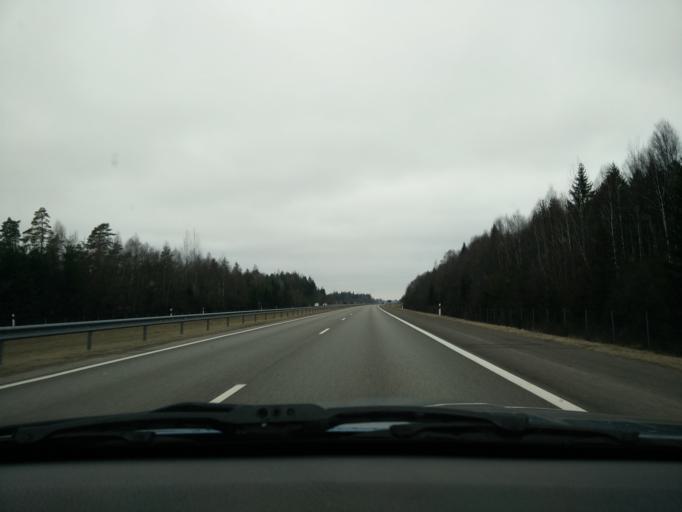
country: LT
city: Rietavas
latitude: 55.6167
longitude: 22.0077
